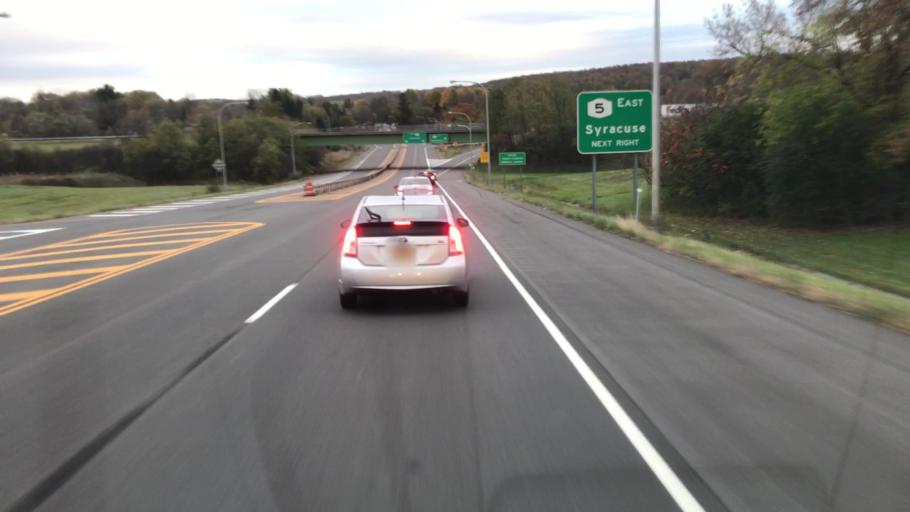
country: US
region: New York
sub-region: Onondaga County
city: Camillus
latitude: 43.0358
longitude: -76.3248
